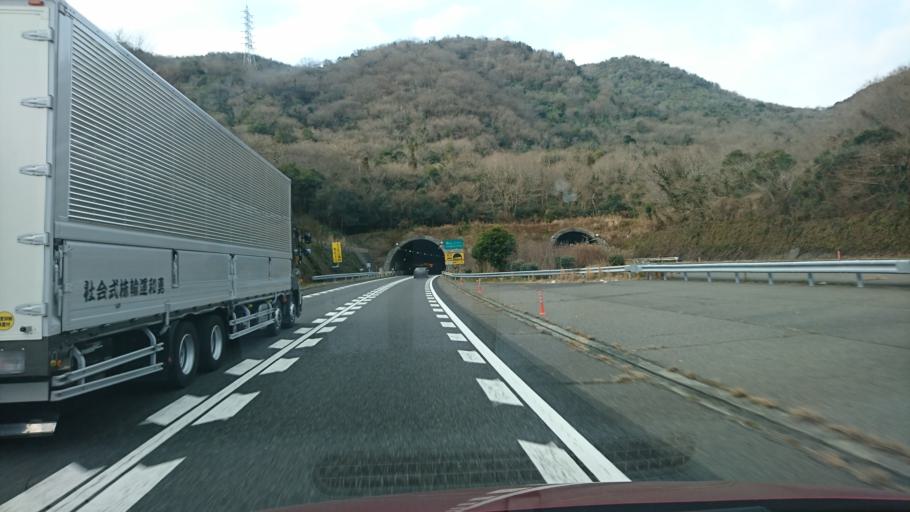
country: JP
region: Hyogo
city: Kariya
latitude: 34.7793
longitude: 134.3945
